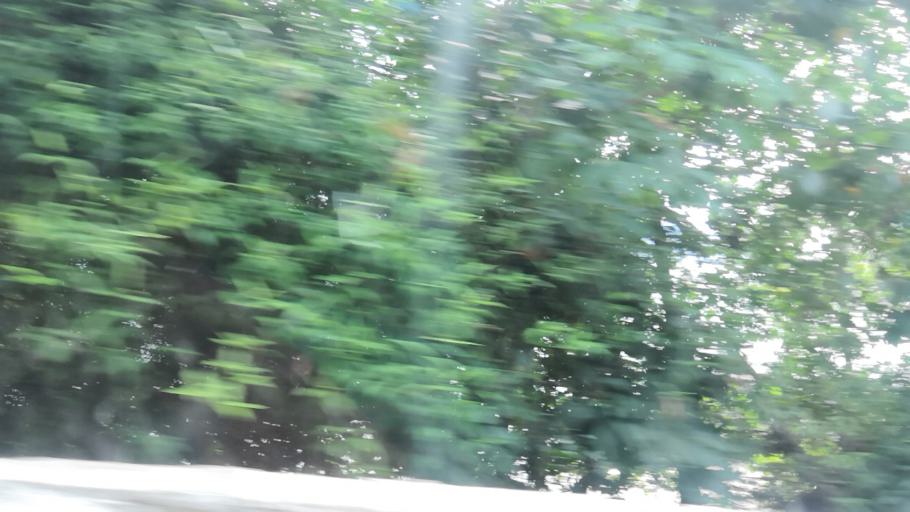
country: MY
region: Perak
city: Lumut
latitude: 4.1958
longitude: 100.5781
